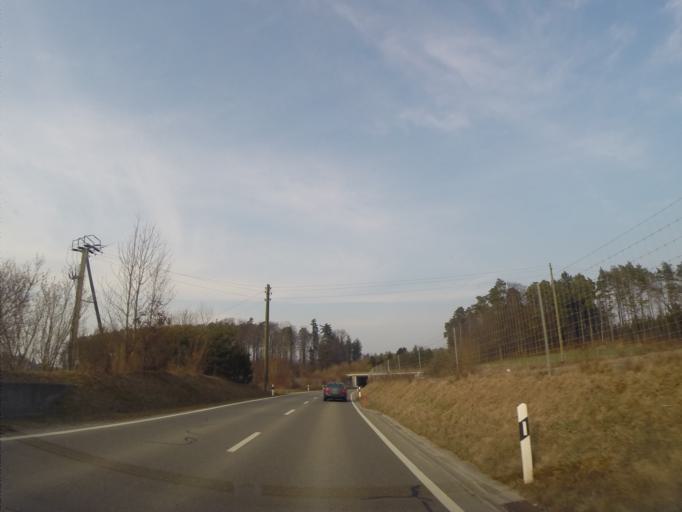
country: CH
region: Zurich
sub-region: Bezirk Andelfingen
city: Henggart
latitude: 47.5543
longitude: 8.6873
